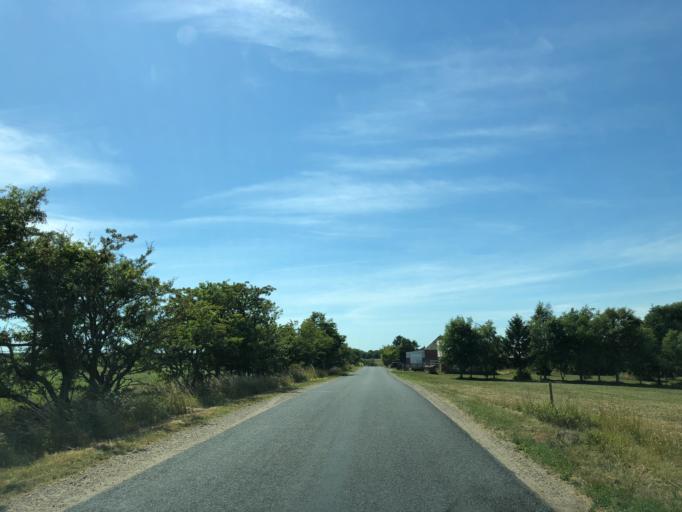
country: DK
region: Central Jutland
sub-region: Skive Kommune
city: Skive
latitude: 56.4624
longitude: 8.9896
